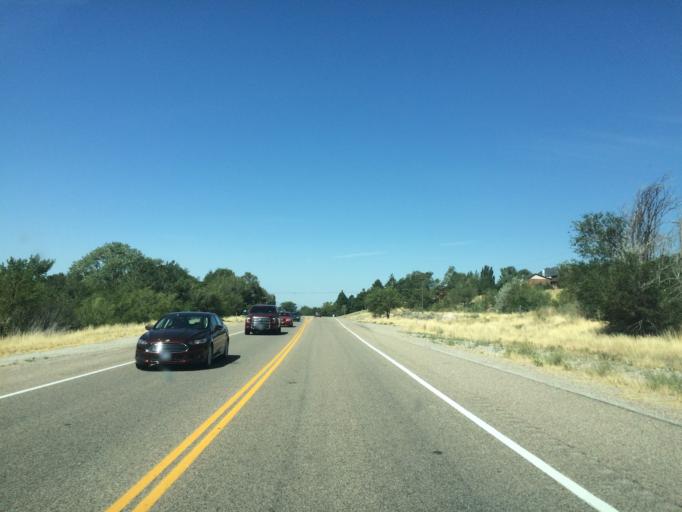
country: US
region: Utah
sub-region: Weber County
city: Ogden
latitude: 41.2388
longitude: -111.9315
